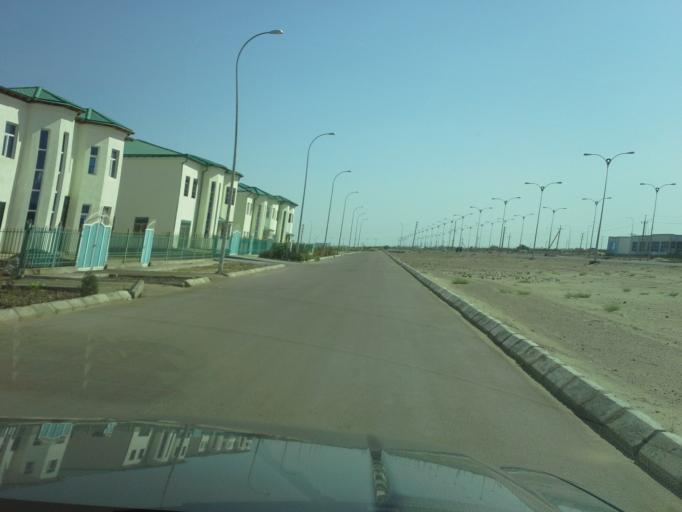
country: TM
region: Dasoguz
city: Dasoguz
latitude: 41.8065
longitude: 59.9523
